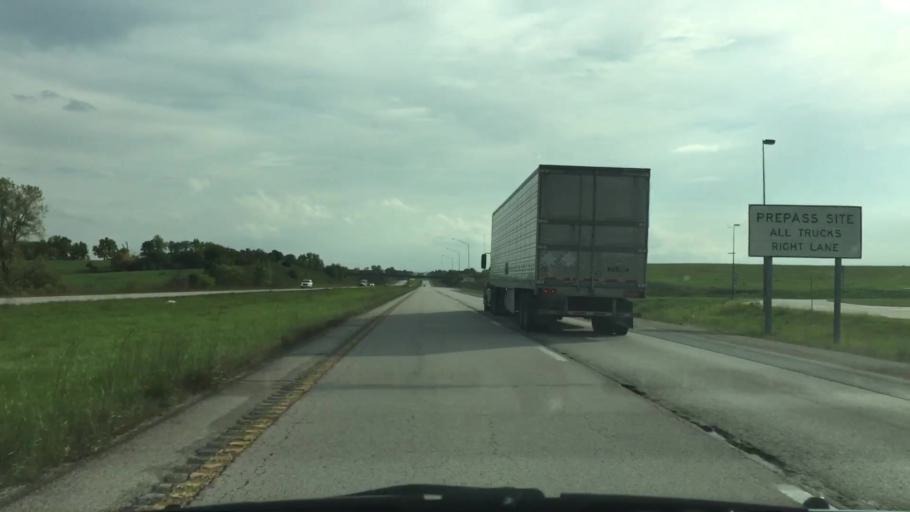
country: US
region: Iowa
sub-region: Decatur County
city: Lamoni
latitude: 40.5493
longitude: -93.9538
